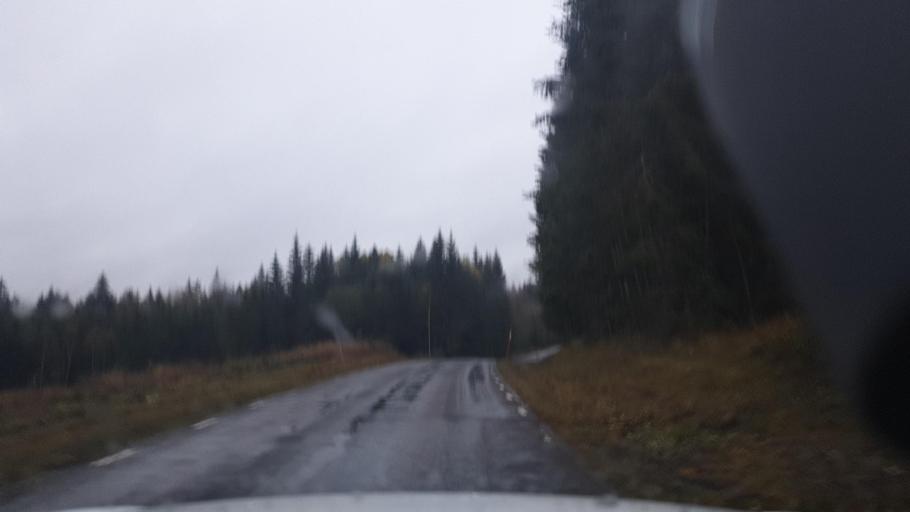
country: SE
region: Vaermland
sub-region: Eda Kommun
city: Amotfors
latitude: 59.8483
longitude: 12.4255
